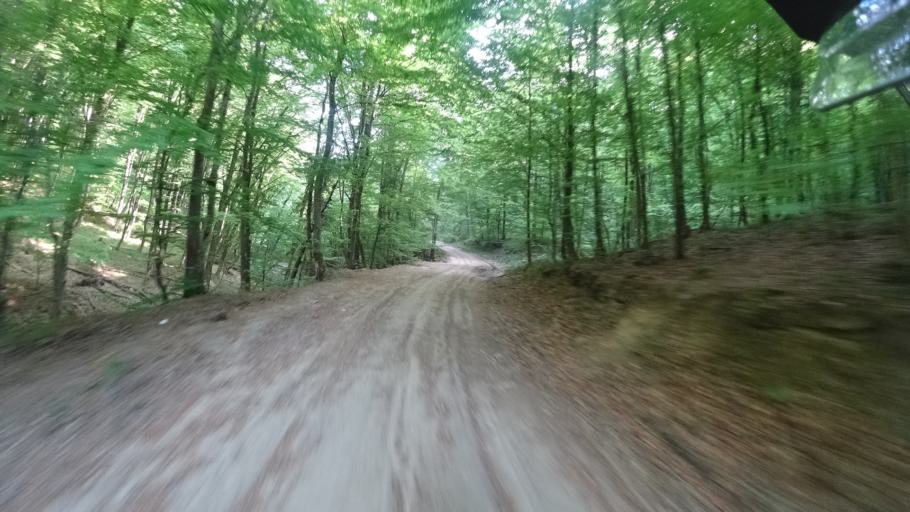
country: HR
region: Zagrebacka
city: Jablanovec
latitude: 45.8669
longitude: 15.8969
